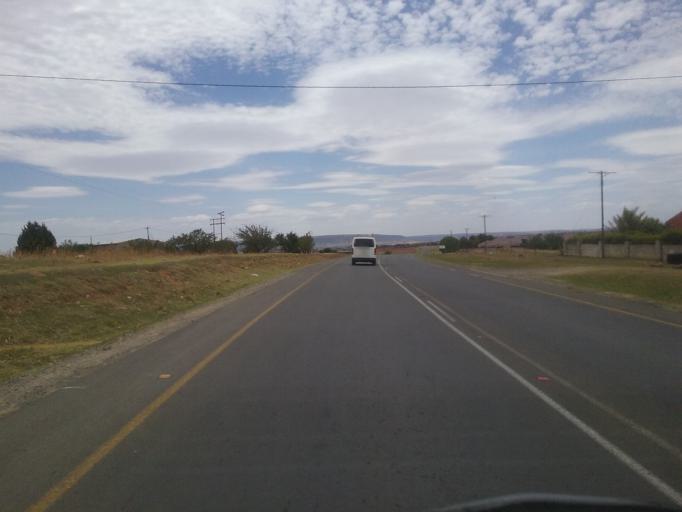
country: LS
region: Maseru
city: Maseru
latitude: -29.4822
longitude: 27.5269
